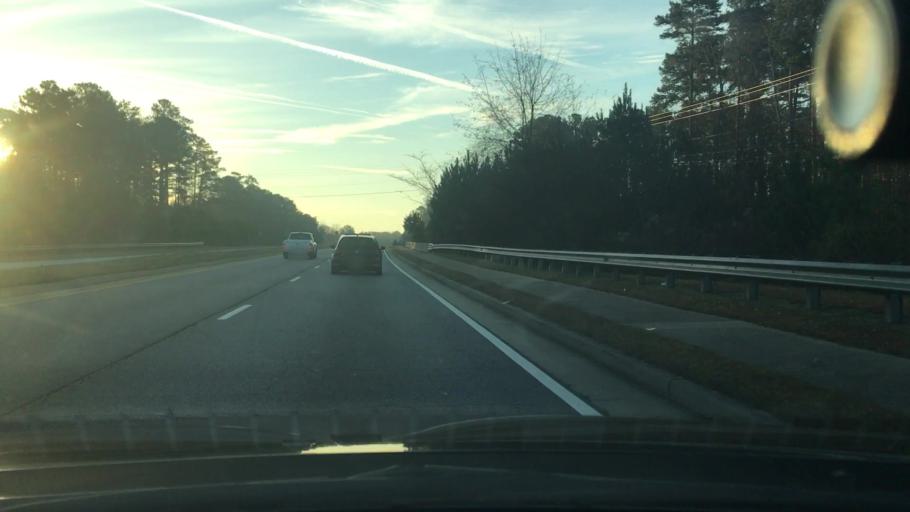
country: US
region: Georgia
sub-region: Fayette County
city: Peachtree City
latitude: 33.3703
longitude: -84.5681
